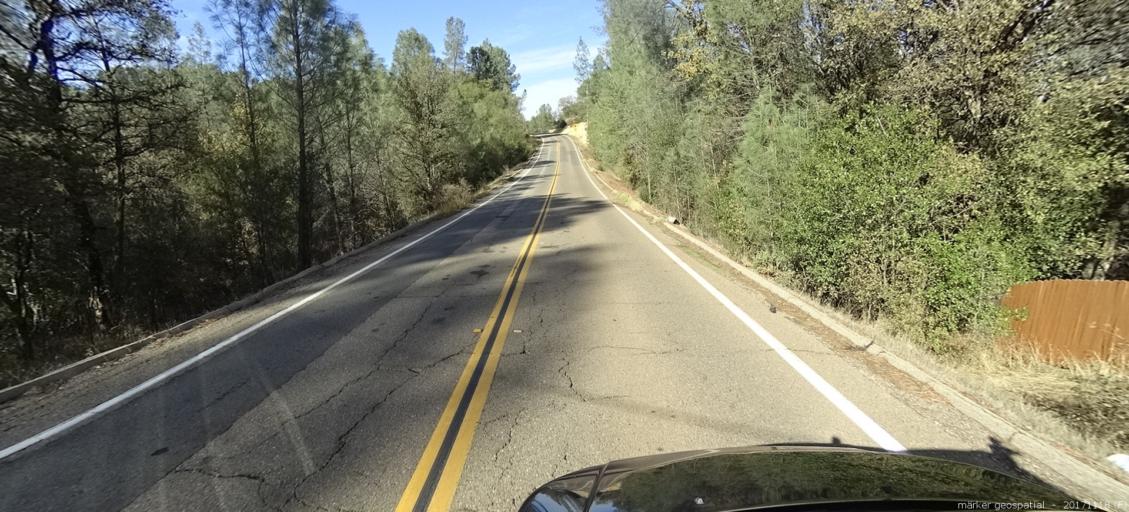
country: US
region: California
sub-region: Shasta County
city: Anderson
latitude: 40.4670
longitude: -122.3970
